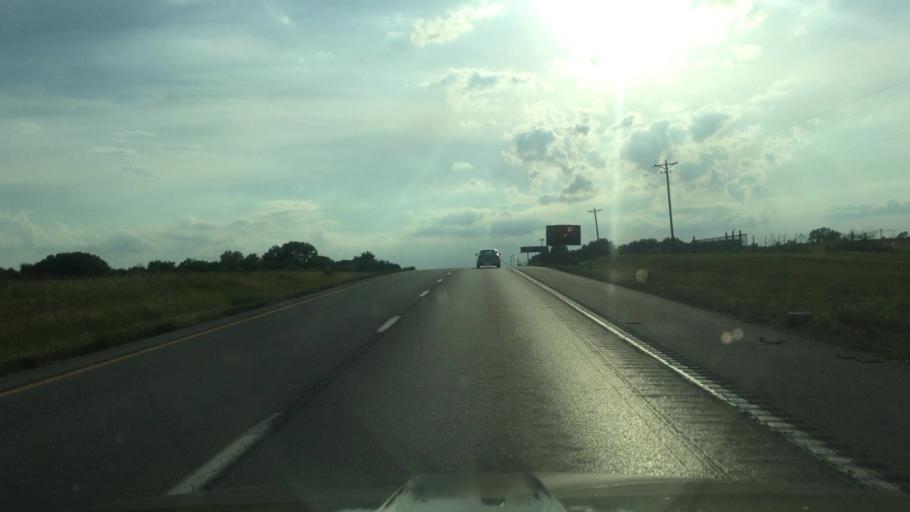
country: US
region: Missouri
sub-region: Jackson County
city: Lone Jack
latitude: 38.8695
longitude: -94.1036
